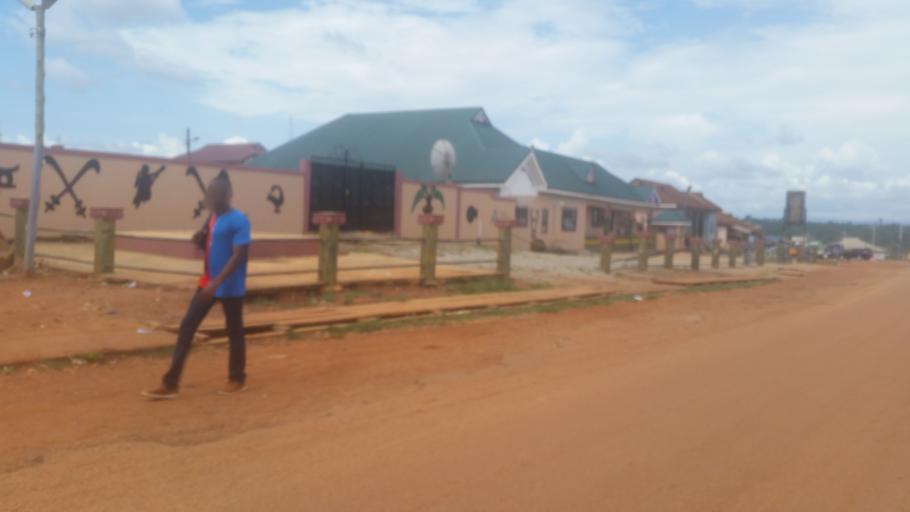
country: GH
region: Western
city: Bibiani
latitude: 6.8039
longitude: -2.5205
